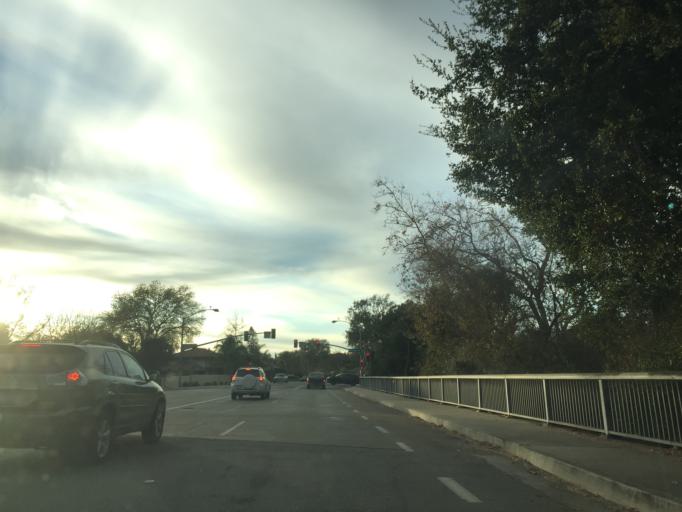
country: US
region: California
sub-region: Santa Barbara County
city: Goleta
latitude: 34.4530
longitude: -119.8133
